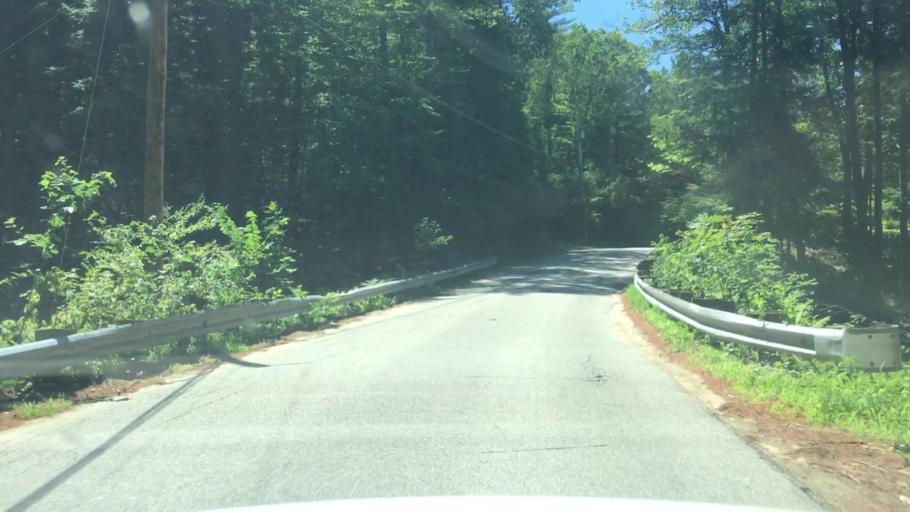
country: US
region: New Hampshire
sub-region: Merrimack County
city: Hopkinton
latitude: 43.2019
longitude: -71.6690
